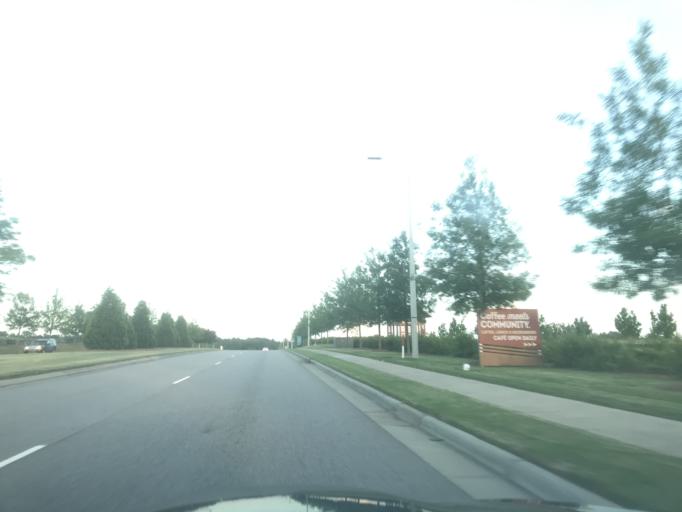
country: US
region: North Carolina
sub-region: Wake County
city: Knightdale
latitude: 35.7722
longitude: -78.4283
